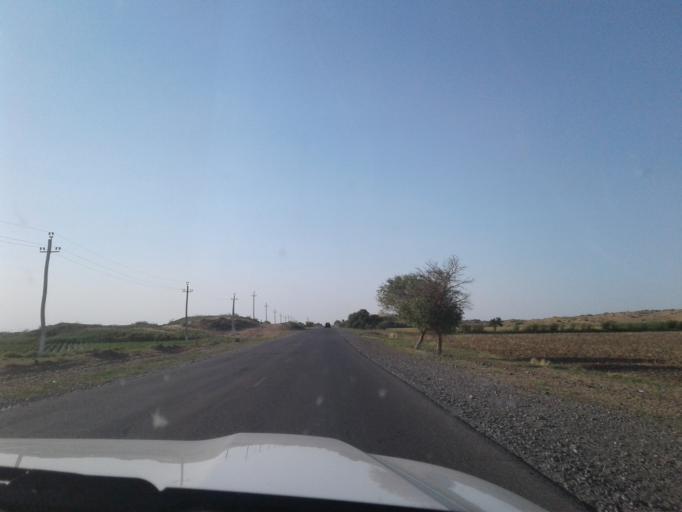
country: TM
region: Mary
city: Yoloeten
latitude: 37.2455
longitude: 62.3682
